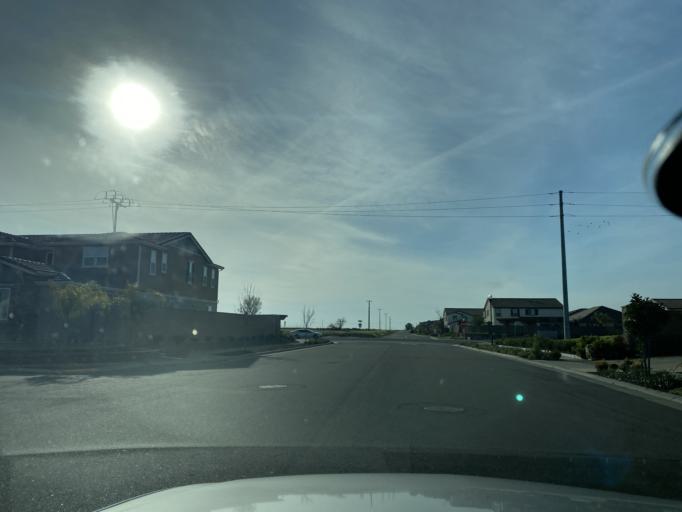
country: US
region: California
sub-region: Sacramento County
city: Elk Grove
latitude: 38.3953
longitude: -121.3923
